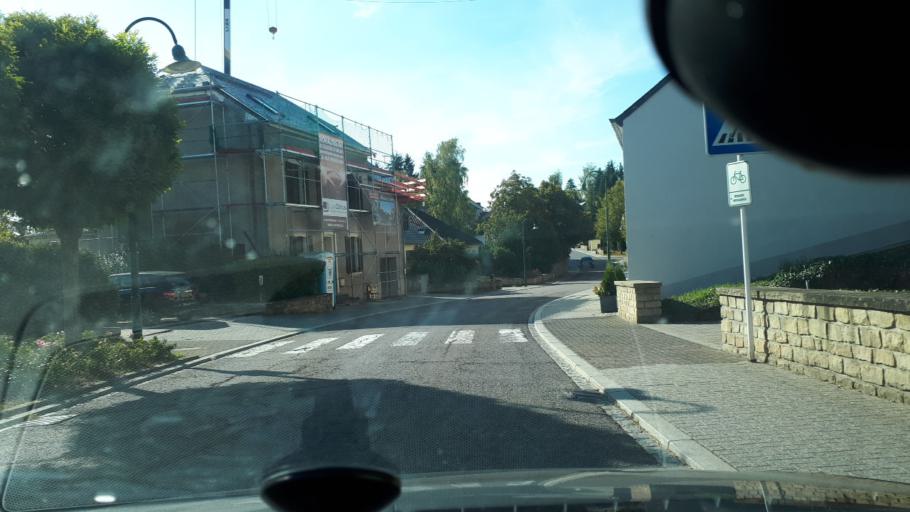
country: LU
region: Grevenmacher
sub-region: Canton de Grevenmacher
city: Flaxweiler
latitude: 49.6683
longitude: 6.3020
